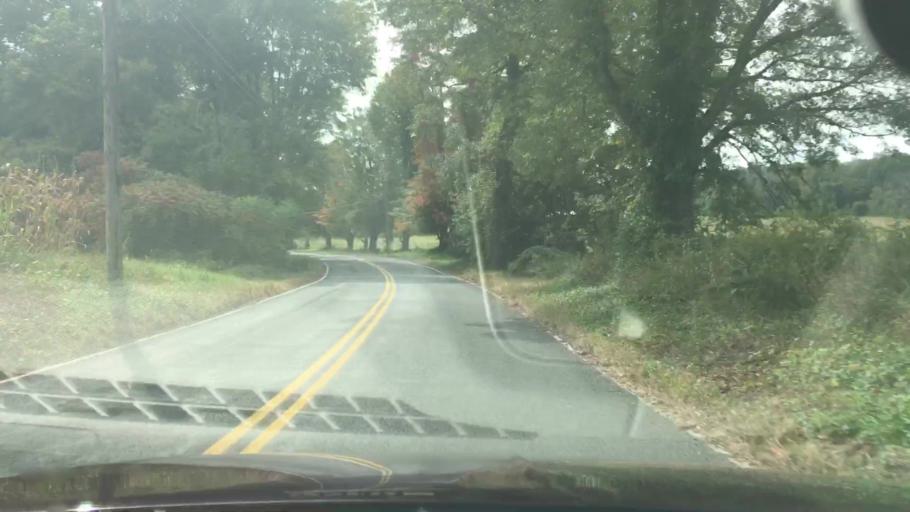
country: US
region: Connecticut
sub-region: Tolland County
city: Somers
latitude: 41.9625
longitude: -72.4832
